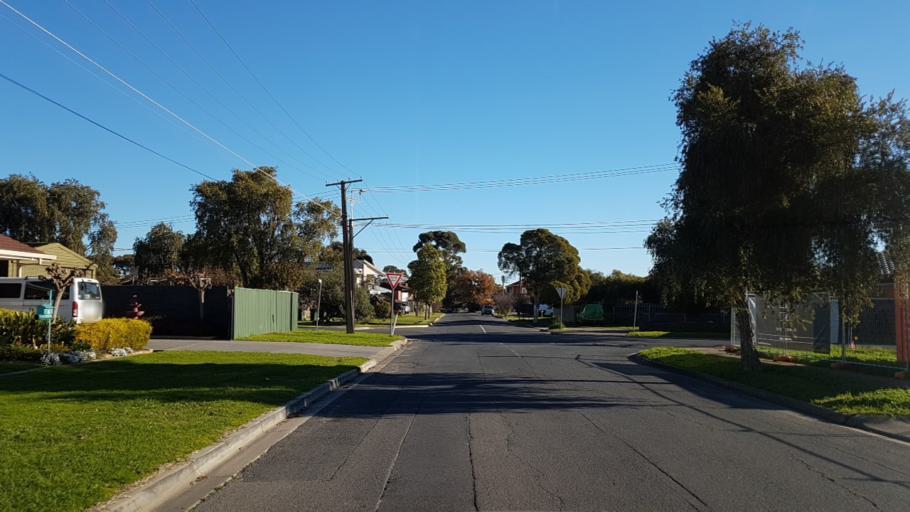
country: AU
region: South Australia
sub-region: Campbelltown
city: Paradise
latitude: -34.8768
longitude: 138.6783
